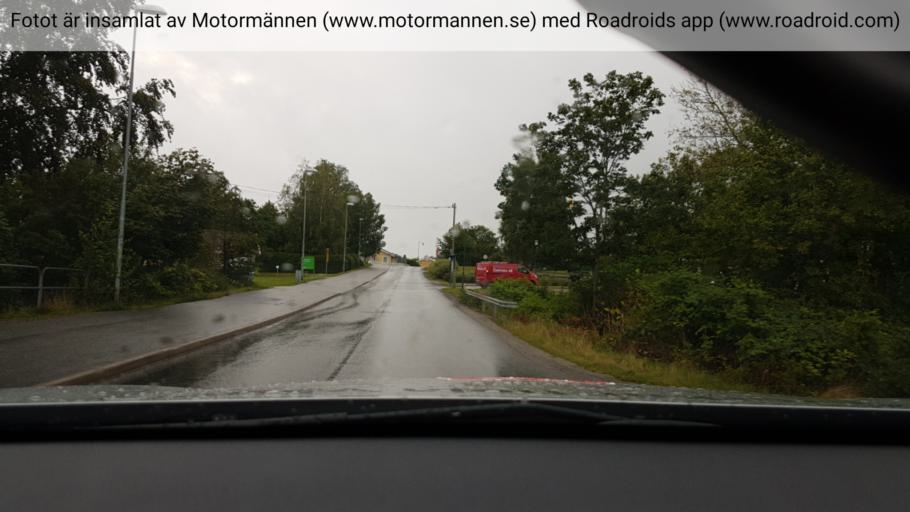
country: SE
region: Stockholm
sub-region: Haninge Kommun
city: Jordbro
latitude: 59.1058
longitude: 18.0409
